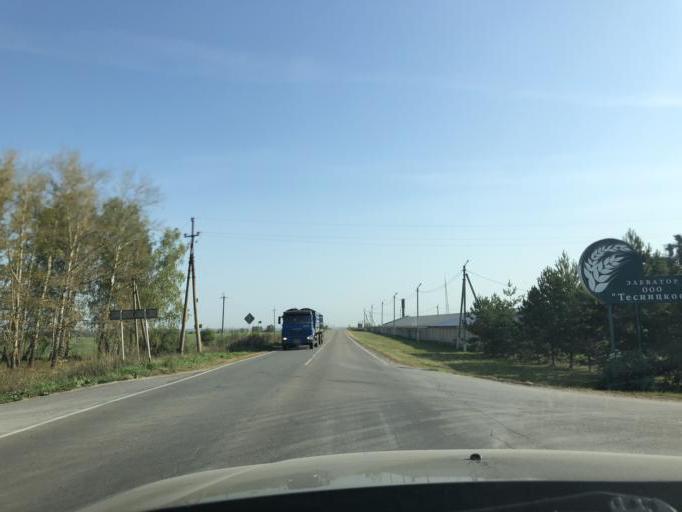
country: RU
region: Tula
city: Novogurovskiy
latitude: 54.4578
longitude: 37.4454
